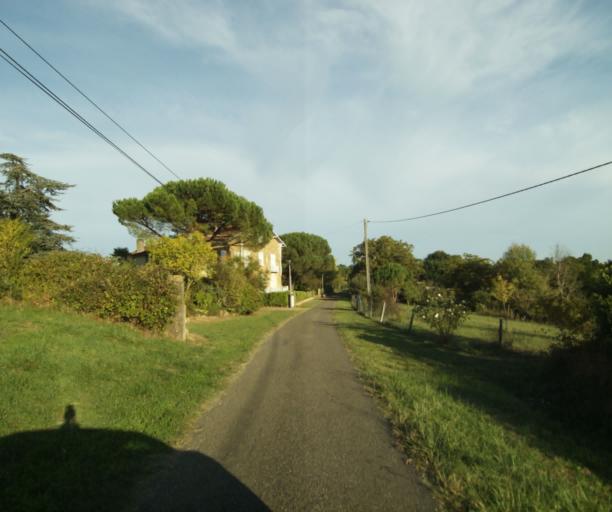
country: FR
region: Midi-Pyrenees
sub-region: Departement du Gers
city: Cazaubon
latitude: 43.8615
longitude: 0.0009
